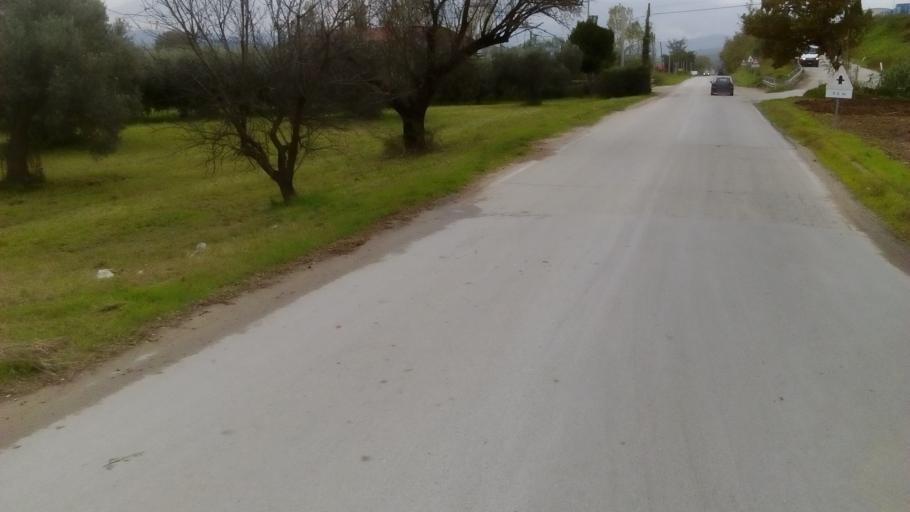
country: IT
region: Abruzzo
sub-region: Provincia di Chieti
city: San Salvo
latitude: 42.0323
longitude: 14.7427
